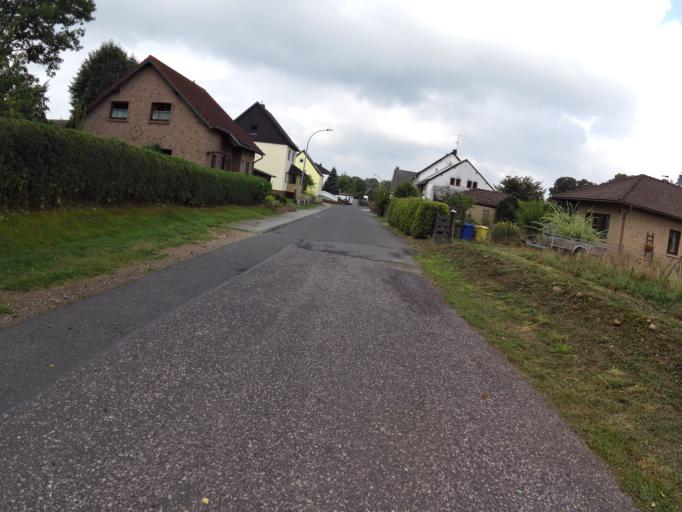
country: DE
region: North Rhine-Westphalia
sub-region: Regierungsbezirk Koln
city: Dahlem
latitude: 50.4162
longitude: 6.5639
